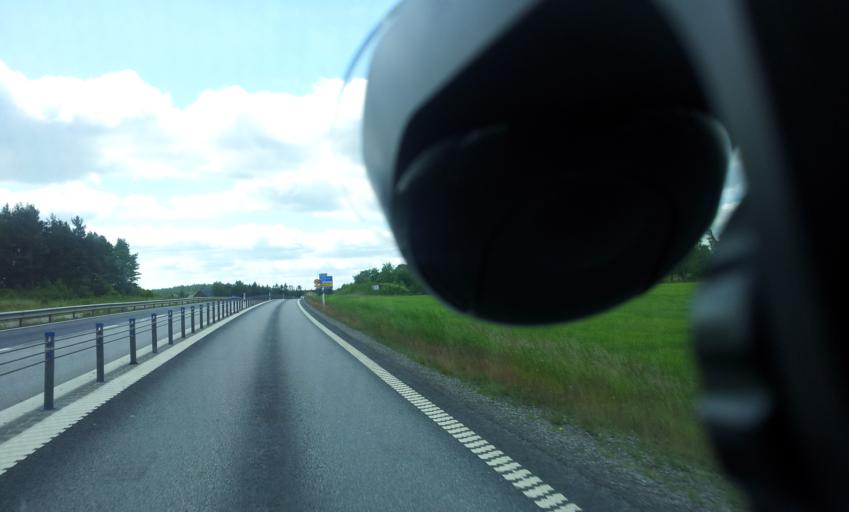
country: SE
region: OEstergoetland
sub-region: Soderkopings Kommun
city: Soederkoeping
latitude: 58.5351
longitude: 16.2829
